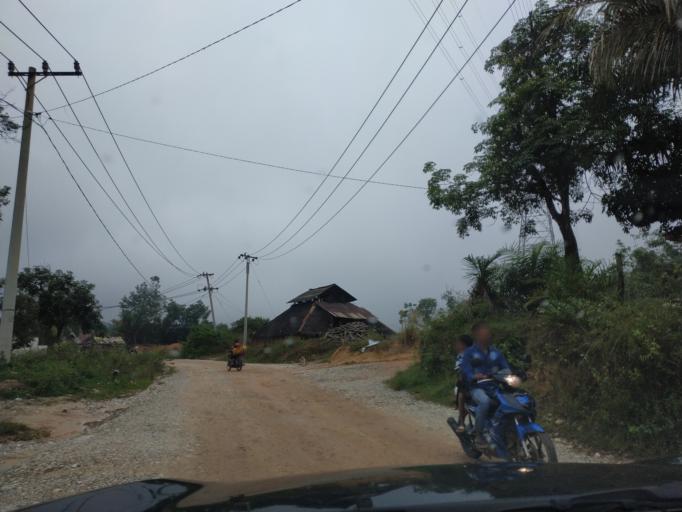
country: ID
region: Riau
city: Pekanbaru
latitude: 0.5040
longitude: 101.5296
